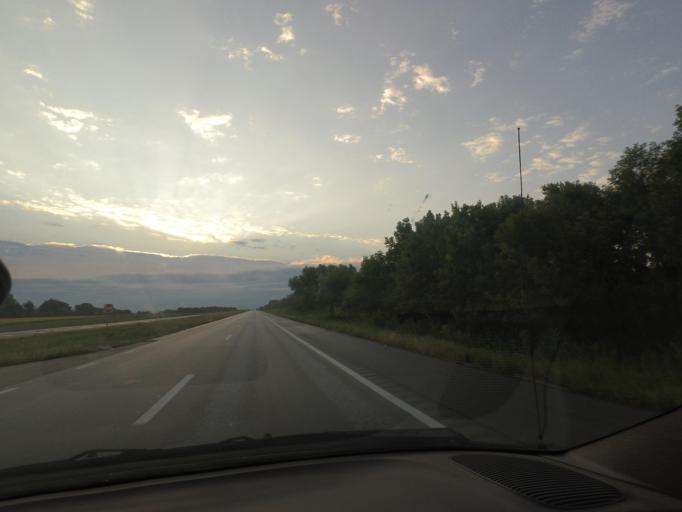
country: US
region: Missouri
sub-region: Shelby County
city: Shelbina
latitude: 39.7350
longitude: -92.2172
